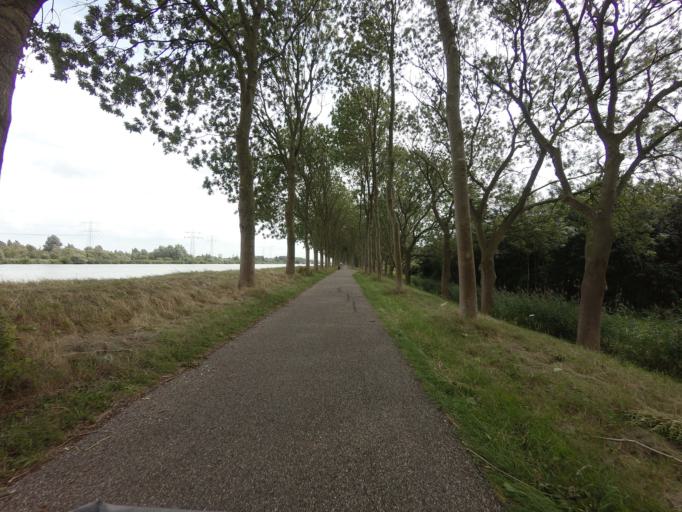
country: NL
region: North Holland
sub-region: Gemeente Diemen
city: Diemen
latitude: 52.3461
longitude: 4.9898
